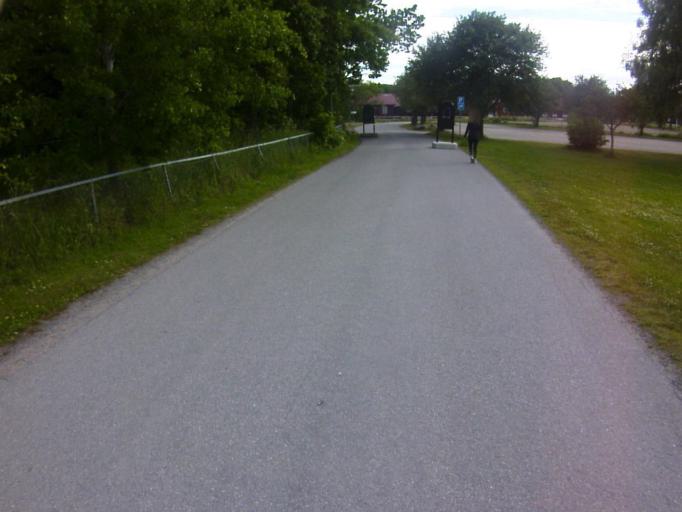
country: SE
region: Soedermanland
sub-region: Eskilstuna Kommun
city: Eskilstuna
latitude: 59.3496
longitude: 16.5059
